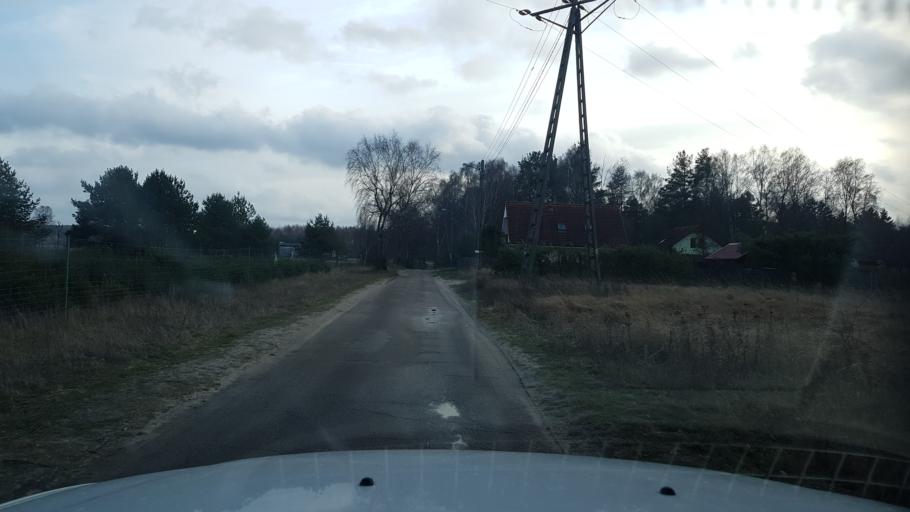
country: PL
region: West Pomeranian Voivodeship
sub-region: Powiat szczecinecki
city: Borne Sulinowo
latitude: 53.6299
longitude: 16.6124
